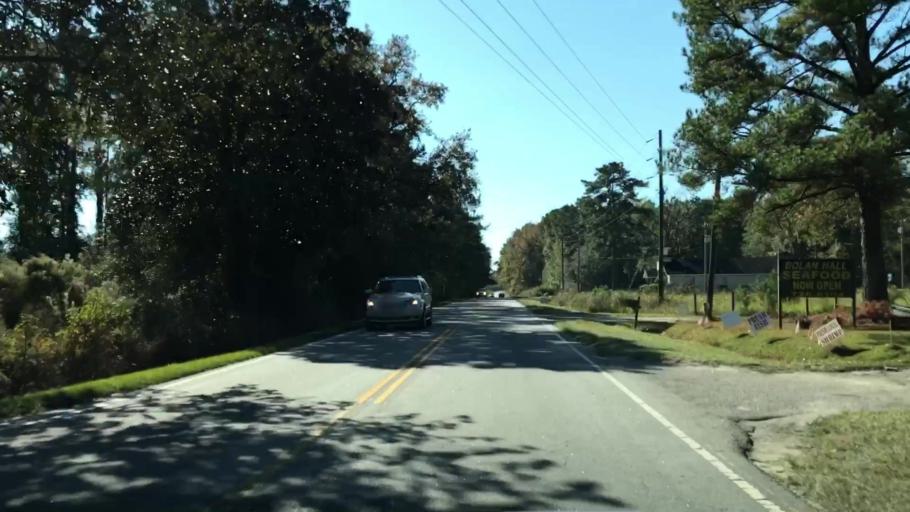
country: US
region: South Carolina
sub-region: Jasper County
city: Ridgeland
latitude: 32.4287
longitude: -80.8962
